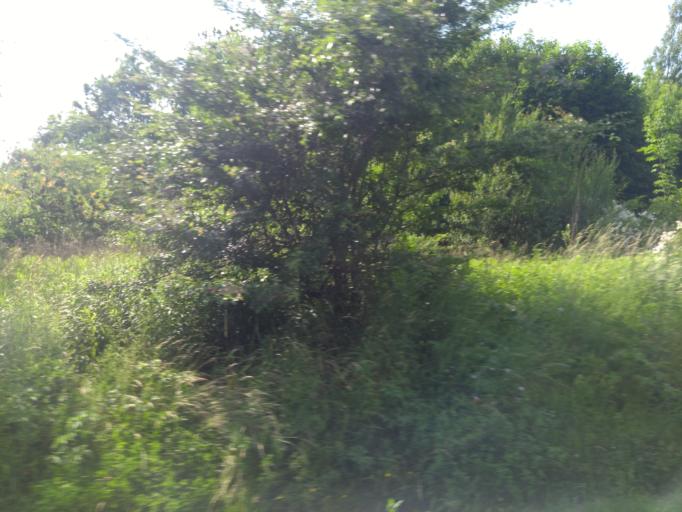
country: PL
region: Lesser Poland Voivodeship
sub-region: Powiat wielicki
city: Kokotow
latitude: 50.0891
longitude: 20.0575
